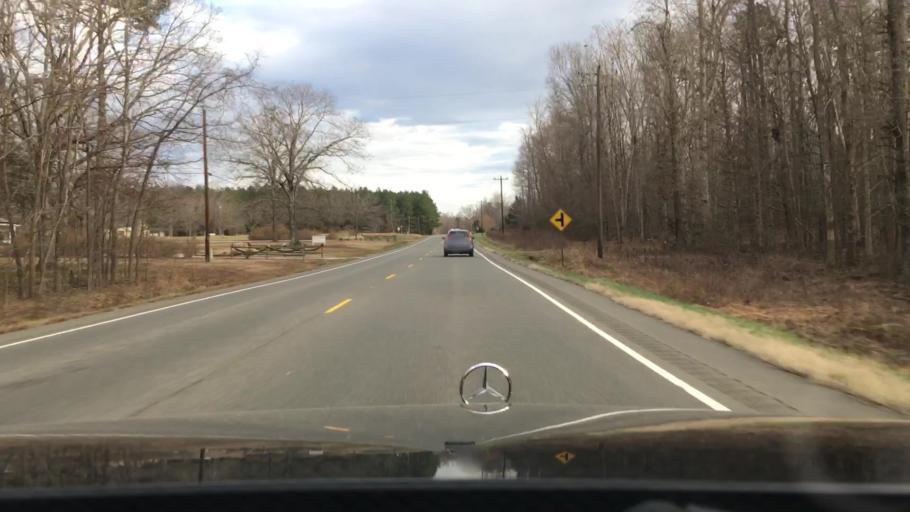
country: US
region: North Carolina
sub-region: Orange County
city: Hillsborough
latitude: 36.2055
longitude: -79.1532
